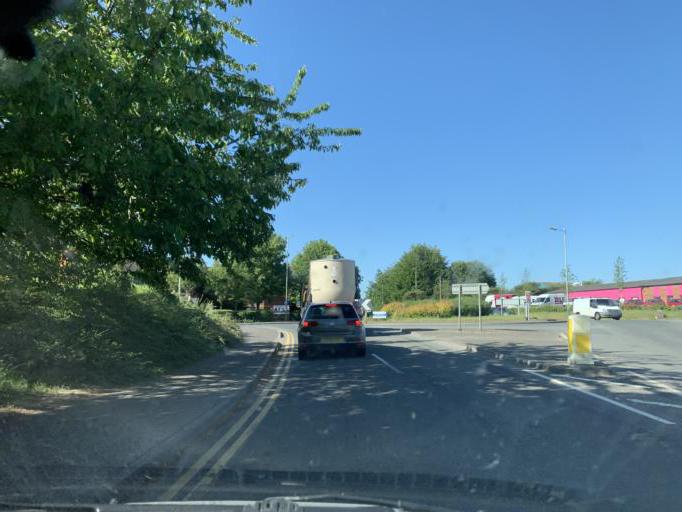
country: GB
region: England
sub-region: Wiltshire
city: Devizes
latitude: 51.3643
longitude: -1.9724
